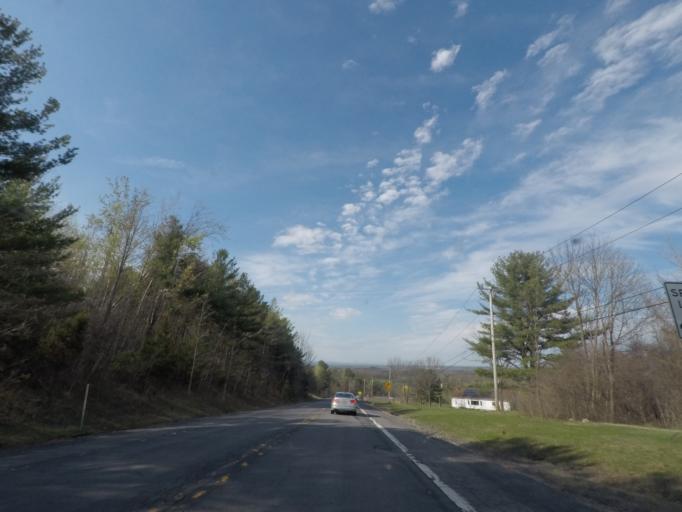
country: US
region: New York
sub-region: Albany County
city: Voorheesville
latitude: 42.6208
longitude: -73.9754
